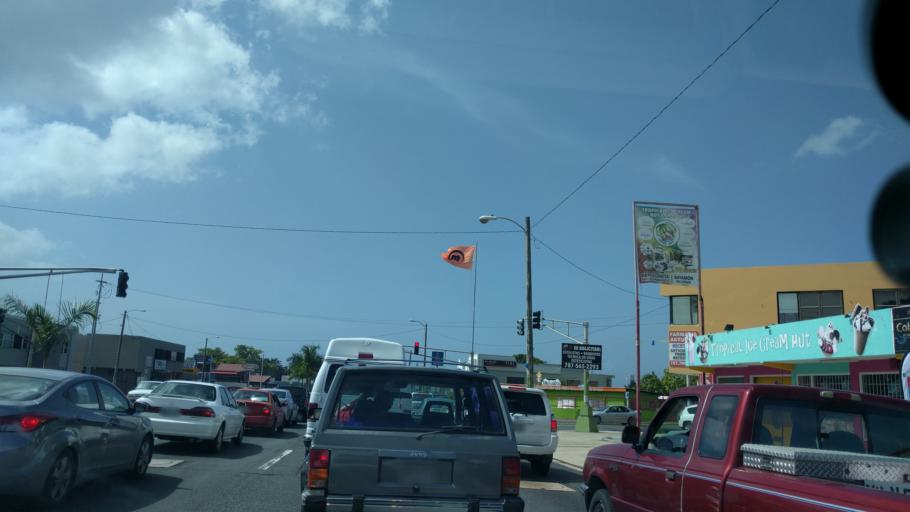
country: PR
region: Bayamon
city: Bayamon
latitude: 18.4175
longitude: -66.1631
